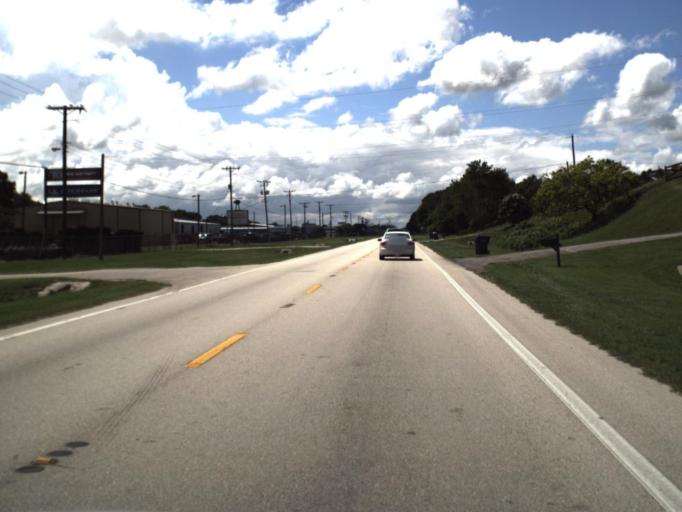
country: US
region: Florida
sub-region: Polk County
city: Mulberry
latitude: 27.8800
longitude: -81.9735
